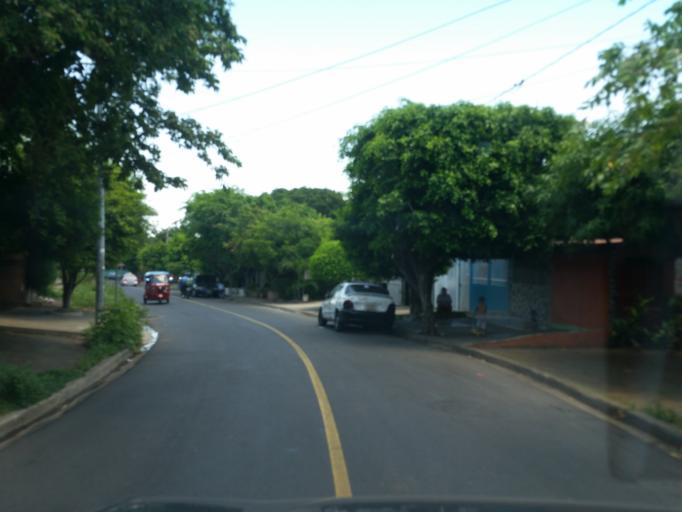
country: NI
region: Managua
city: Managua
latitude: 12.1218
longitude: -86.2413
